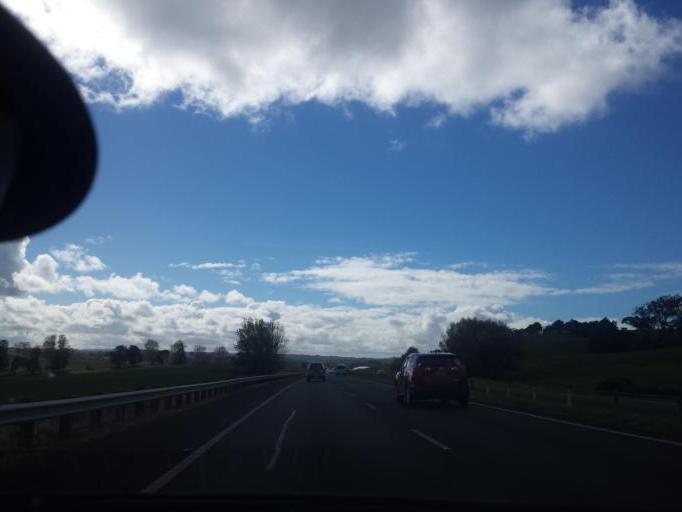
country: NZ
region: Auckland
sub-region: Auckland
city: Rothesay Bay
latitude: -36.6469
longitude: 174.6625
